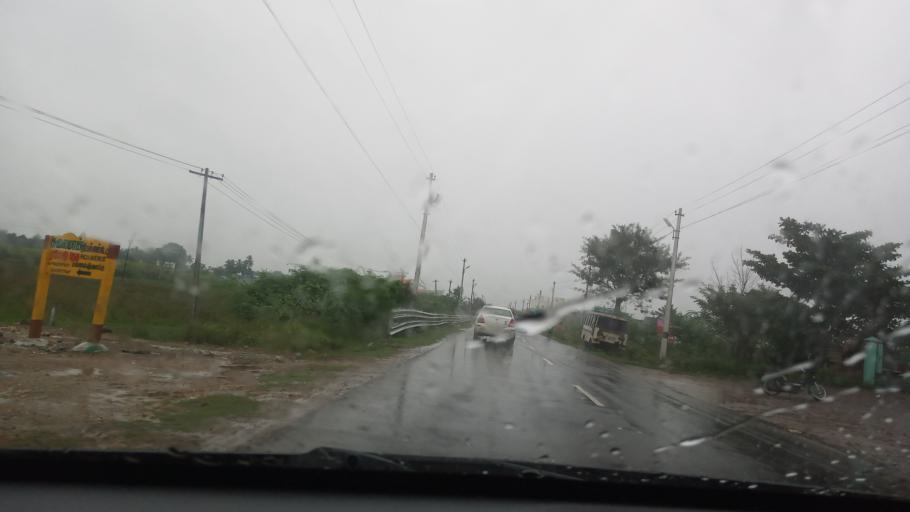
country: IN
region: Tamil Nadu
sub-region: Tiruvannamalai
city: Cheyyar
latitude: 12.6586
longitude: 79.5372
